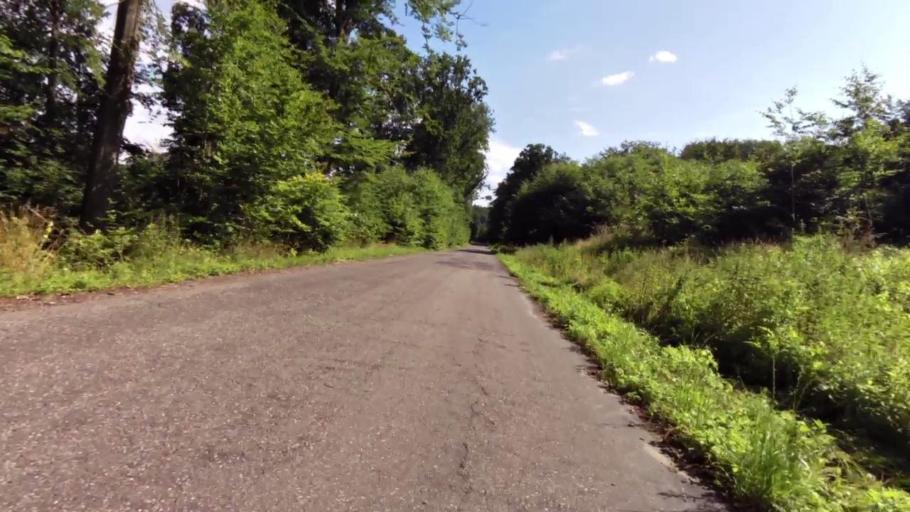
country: PL
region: West Pomeranian Voivodeship
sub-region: Powiat stargardzki
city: Dobrzany
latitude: 53.3836
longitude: 15.4478
